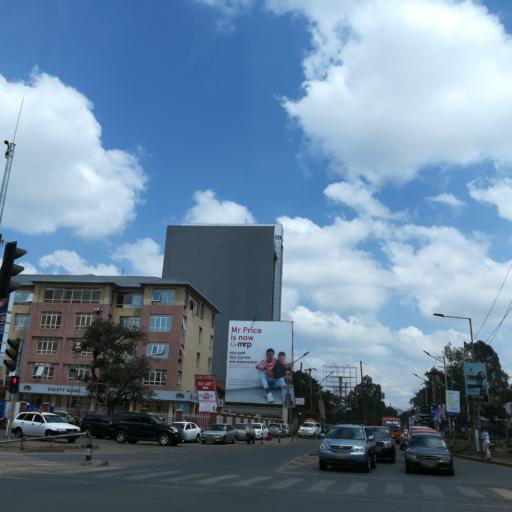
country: KE
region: Nairobi Area
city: Nairobi
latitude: -1.2922
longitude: 36.7871
